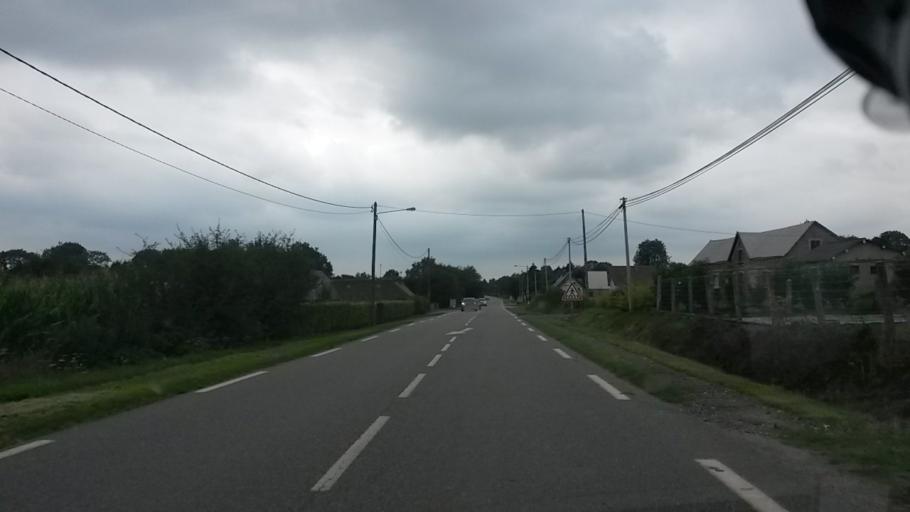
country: FR
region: Haute-Normandie
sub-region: Departement de la Seine-Maritime
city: Gaillefontaine
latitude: 49.7036
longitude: 1.6560
